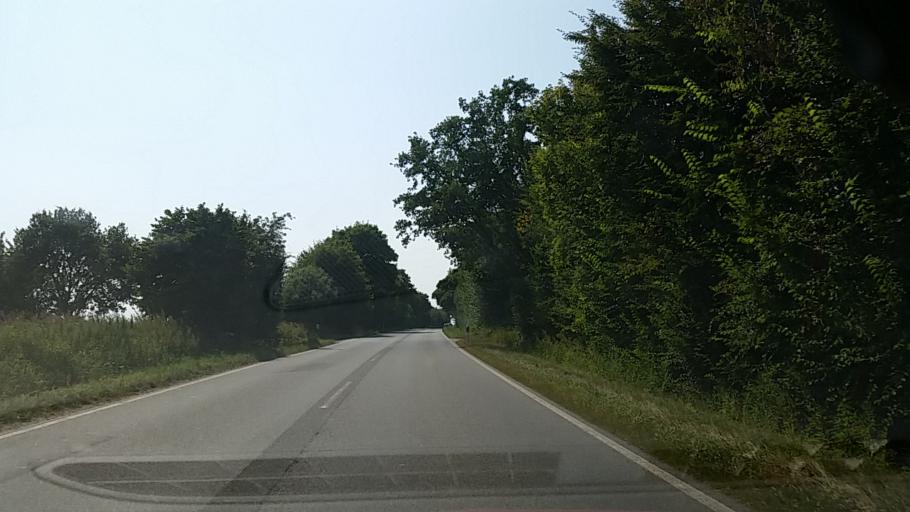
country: DE
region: Schleswig-Holstein
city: Muhlenrade
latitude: 53.5923
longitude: 10.4800
